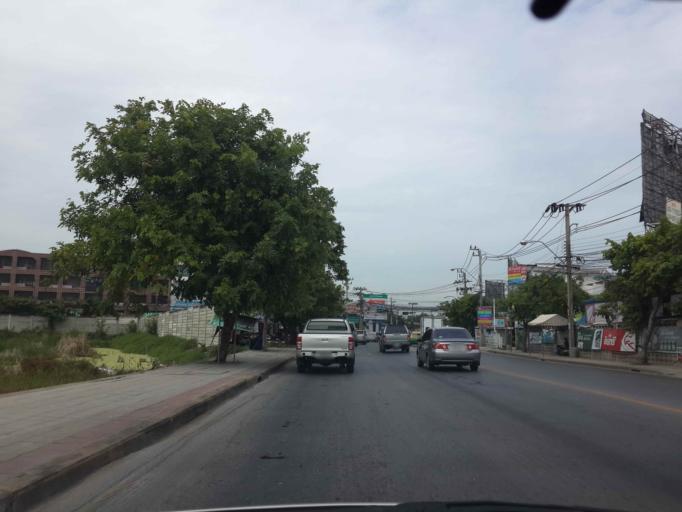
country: TH
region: Bangkok
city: Bang Khen
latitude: 13.8679
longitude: 100.6468
